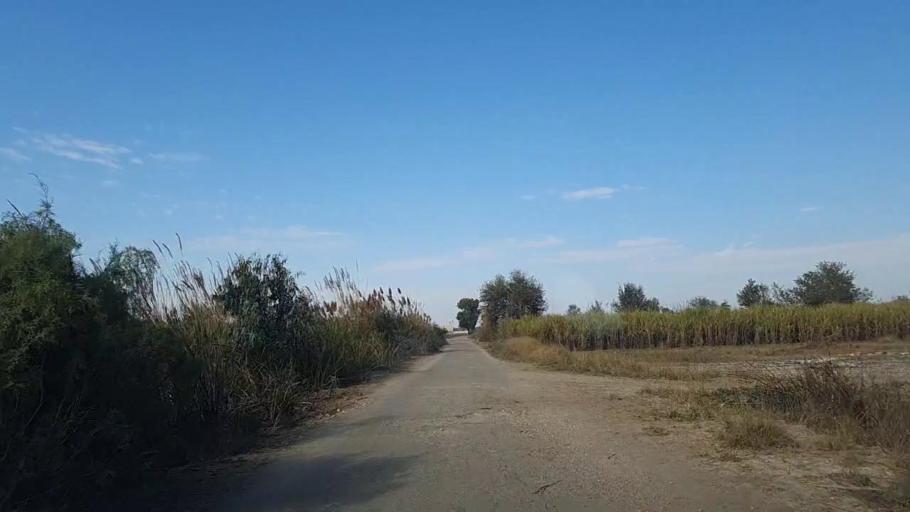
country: PK
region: Sindh
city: Khadro
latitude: 26.2925
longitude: 68.8201
